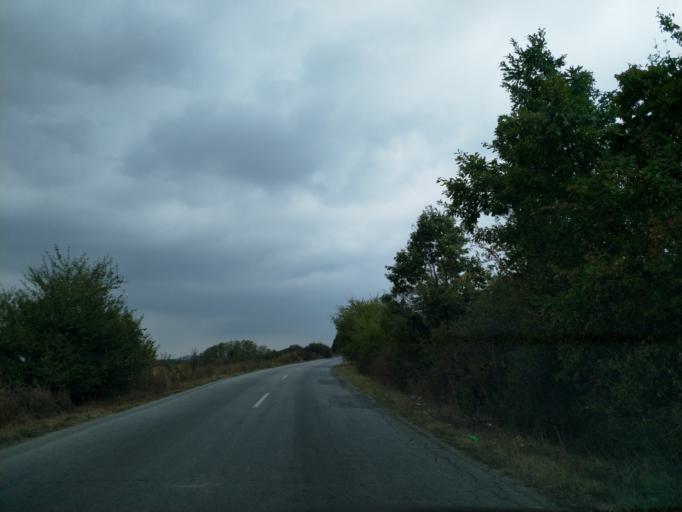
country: RS
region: Central Serbia
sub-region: Pomoravski Okrug
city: Jagodina
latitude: 44.0109
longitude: 21.2011
